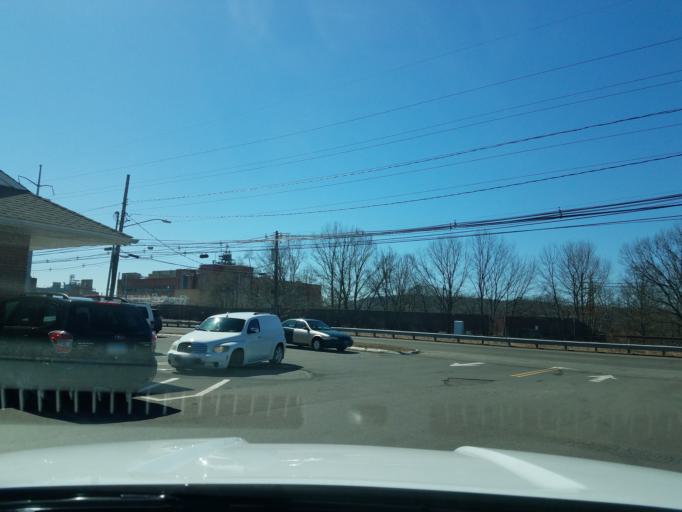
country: US
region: Connecticut
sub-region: New Haven County
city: Wallingford Center
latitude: 41.4370
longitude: -72.8332
